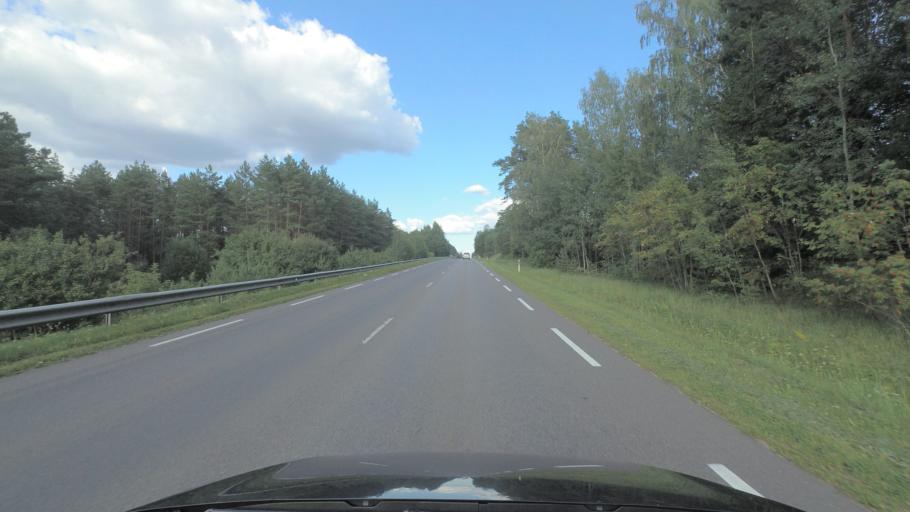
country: LT
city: Pabrade
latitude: 54.9727
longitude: 25.7353
